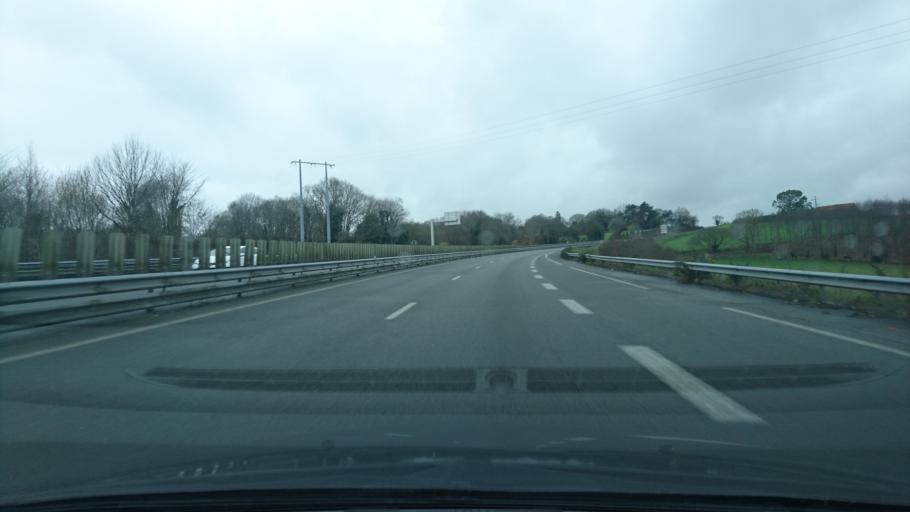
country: FR
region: Brittany
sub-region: Departement du Finistere
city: Taule
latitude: 48.5831
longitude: -3.8740
